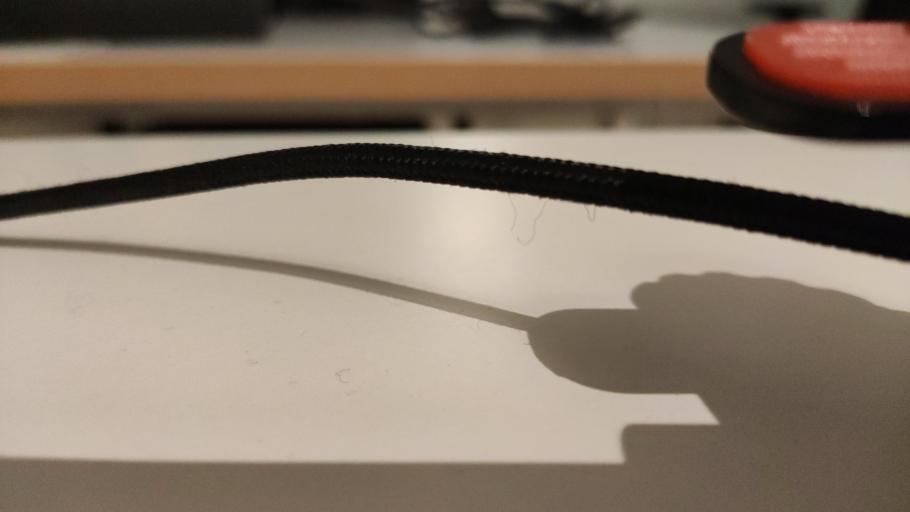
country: RU
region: Moskovskaya
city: Rogachevo
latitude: 56.4067
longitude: 37.2405
